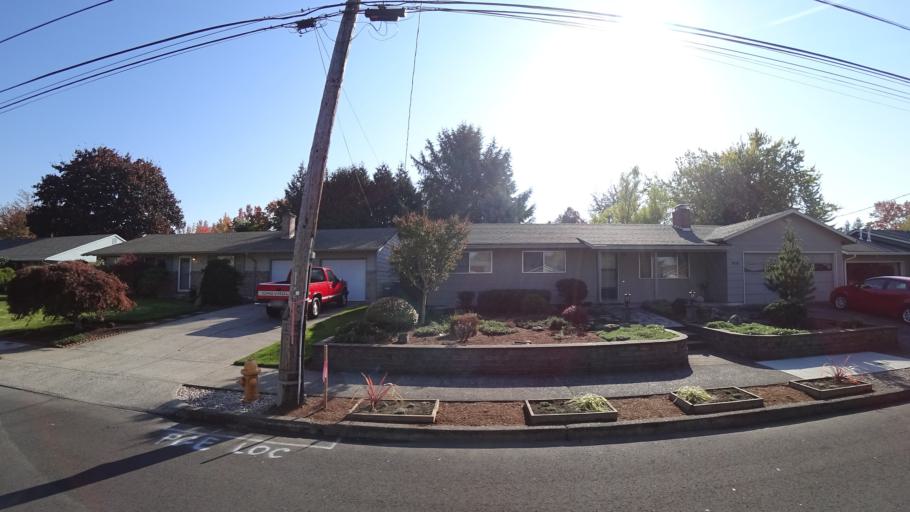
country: US
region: Oregon
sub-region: Multnomah County
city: Gresham
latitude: 45.5015
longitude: -122.4518
